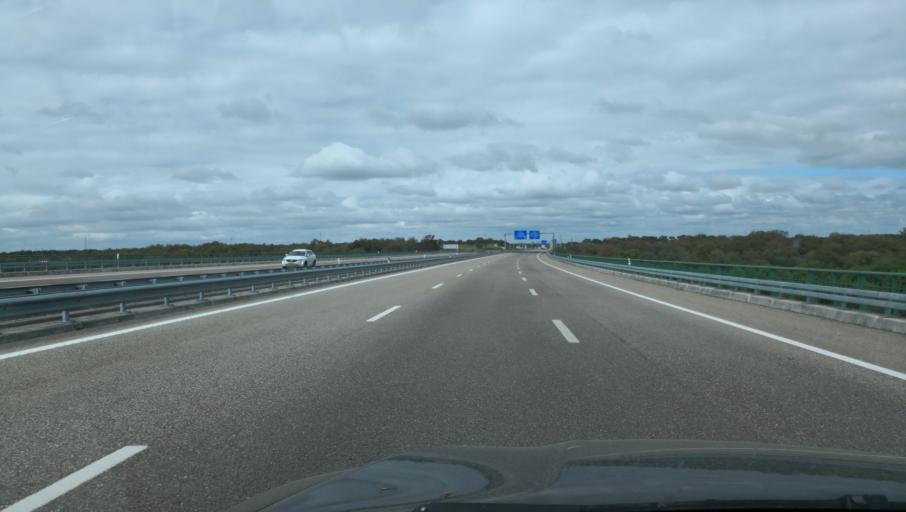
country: PT
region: Santarem
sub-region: Benavente
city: Poceirao
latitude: 38.8917
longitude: -8.7911
